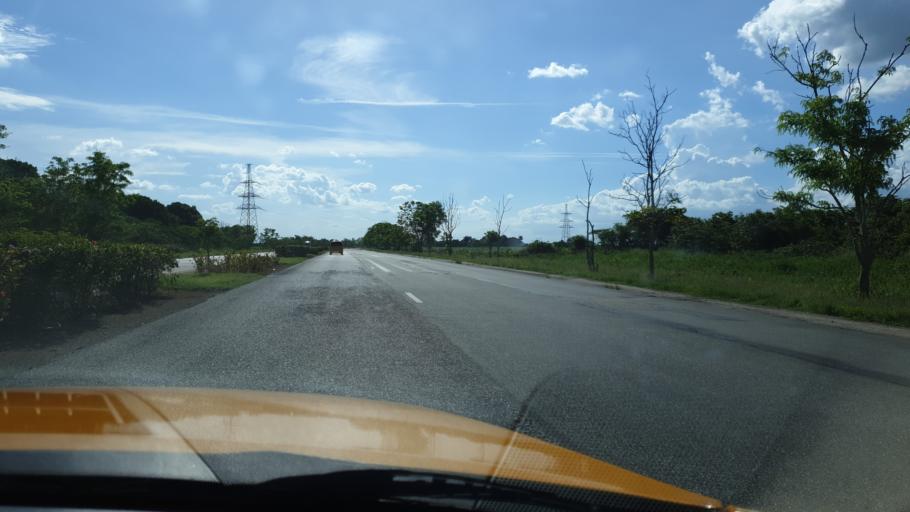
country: CU
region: Cienfuegos
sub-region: Municipio de Aguada de Pasajeros
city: Aguada de Pasajeros
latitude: 22.4083
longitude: -80.8837
